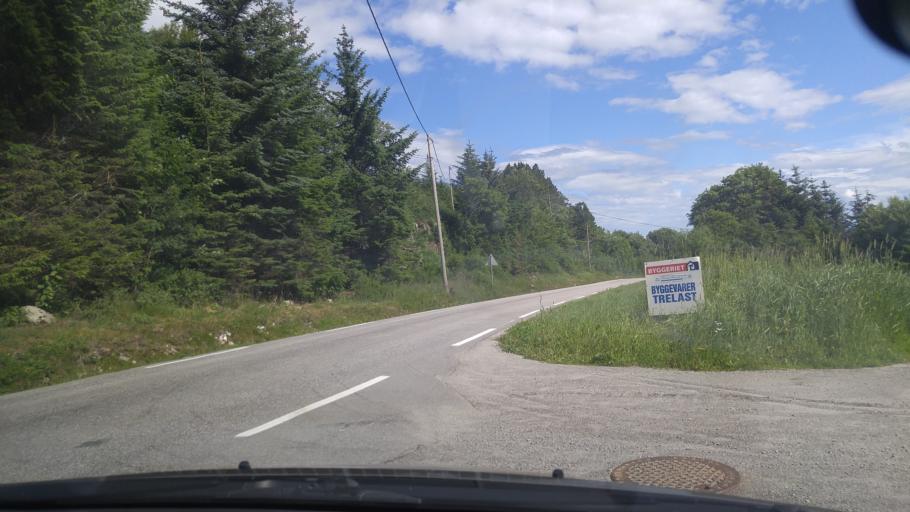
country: NO
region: Nord-Trondelag
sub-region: Vikna
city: Rorvik
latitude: 64.9029
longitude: 11.2530
